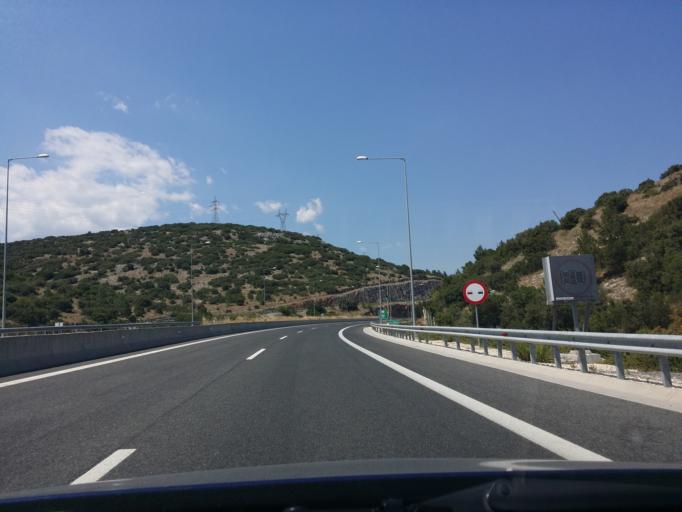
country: GR
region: Peloponnese
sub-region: Nomos Arkadias
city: Tripoli
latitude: 37.4399
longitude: 22.3112
